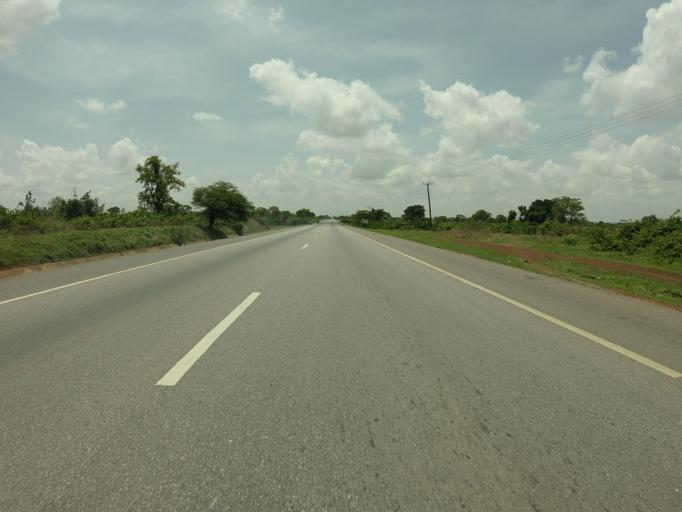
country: GH
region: Northern
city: Tamale
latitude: 9.2933
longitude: -0.9718
